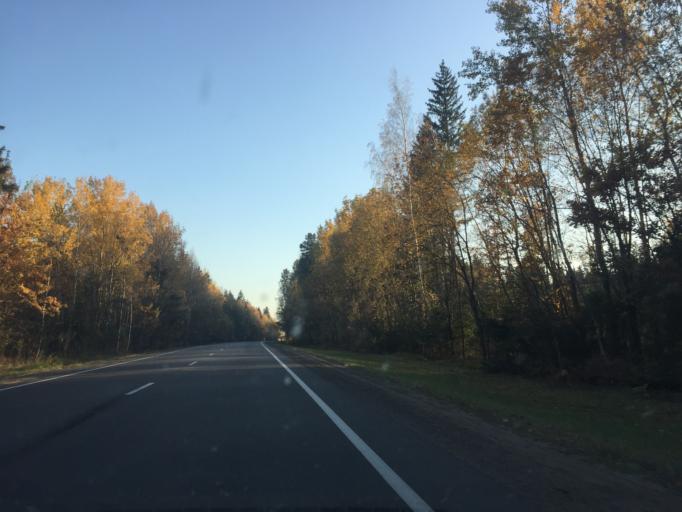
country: BY
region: Mogilev
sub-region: Mahilyowski Rayon
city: Kadino
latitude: 53.8901
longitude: 30.4865
